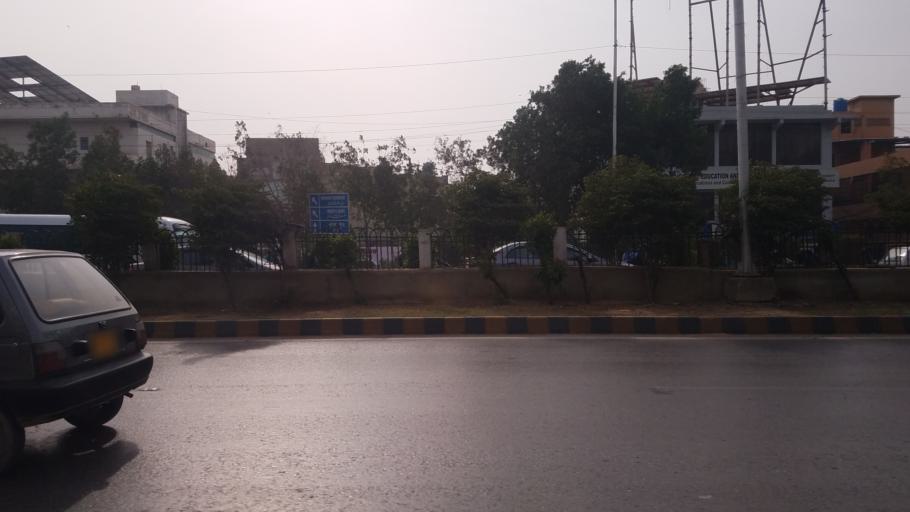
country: PK
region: Sindh
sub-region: Karachi District
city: Karachi
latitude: 24.8600
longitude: 67.0603
